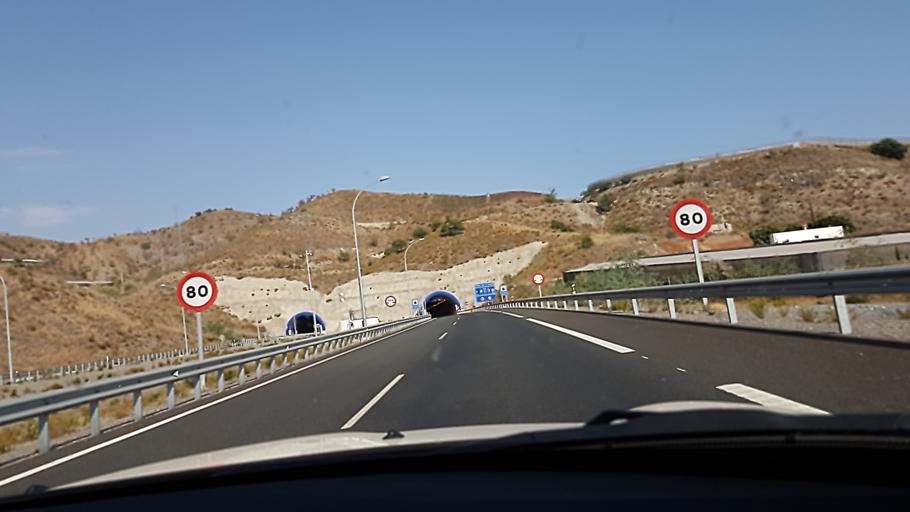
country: ES
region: Andalusia
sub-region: Provincia de Granada
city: Polopos
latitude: 36.7505
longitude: -3.3031
